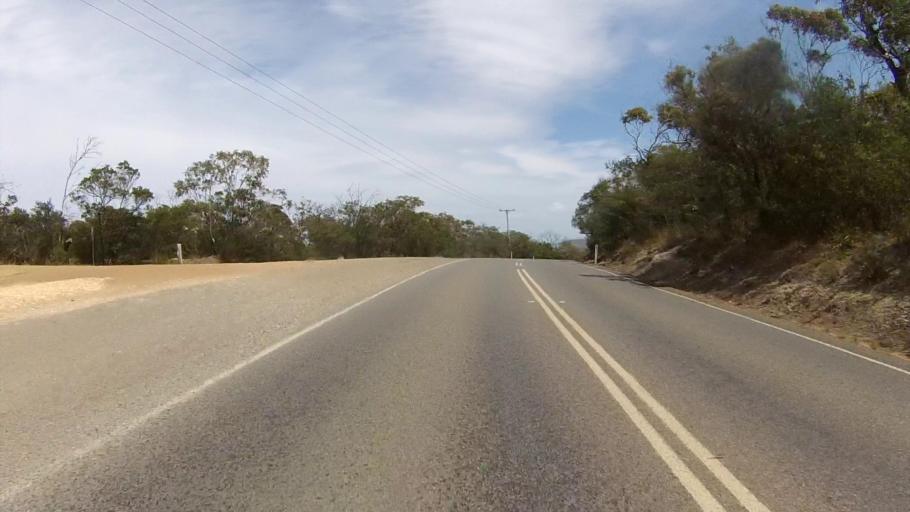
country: AU
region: Tasmania
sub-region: Clarence
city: Sandford
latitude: -43.0263
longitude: 147.4815
